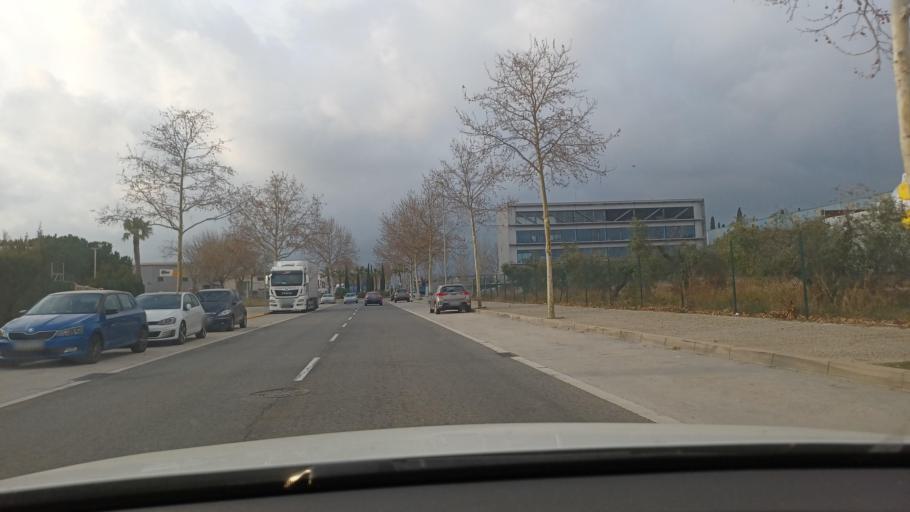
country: ES
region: Catalonia
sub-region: Provincia de Tarragona
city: Vila-seca
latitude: 41.1158
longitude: 1.1535
